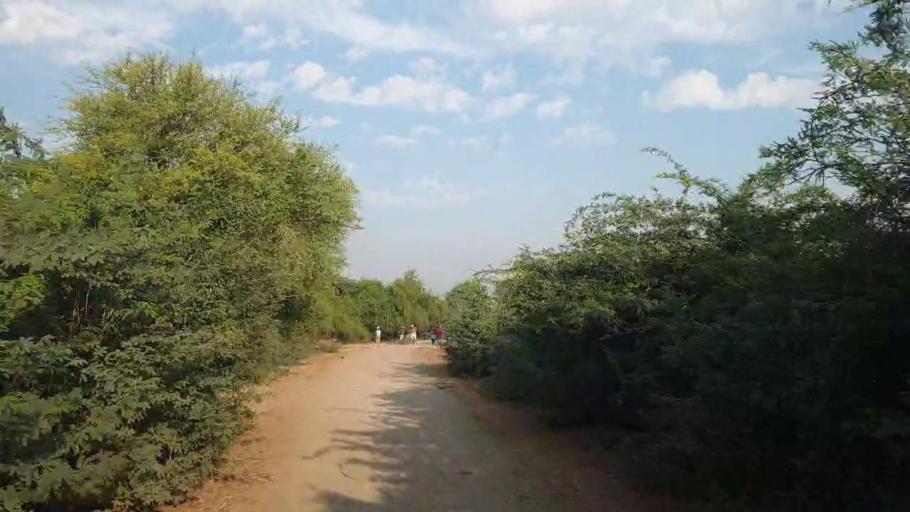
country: PK
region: Sindh
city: Tando Bago
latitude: 24.8061
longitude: 68.9588
